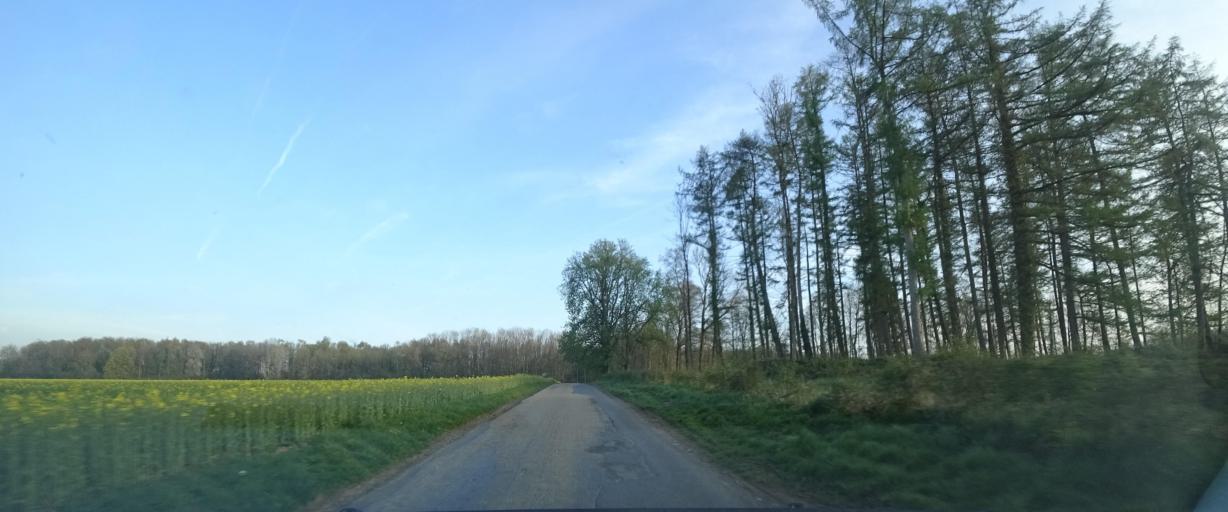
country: BE
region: Wallonia
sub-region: Province de Namur
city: Hamois
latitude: 50.3130
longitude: 5.1547
